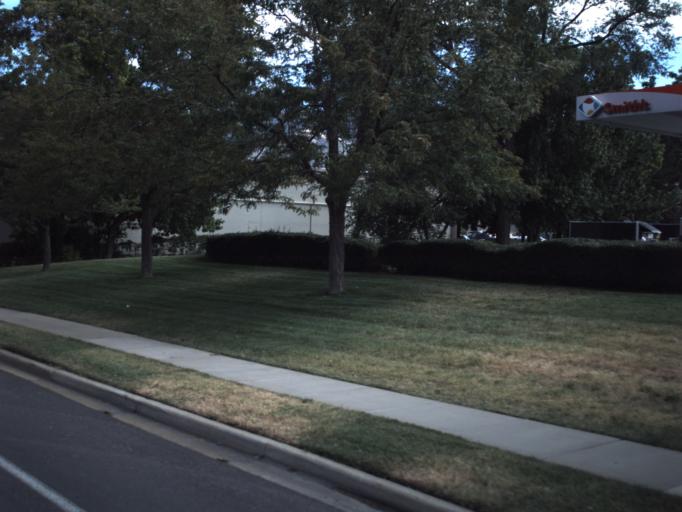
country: US
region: Utah
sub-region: Davis County
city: Bountiful
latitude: 40.8826
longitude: -111.8856
